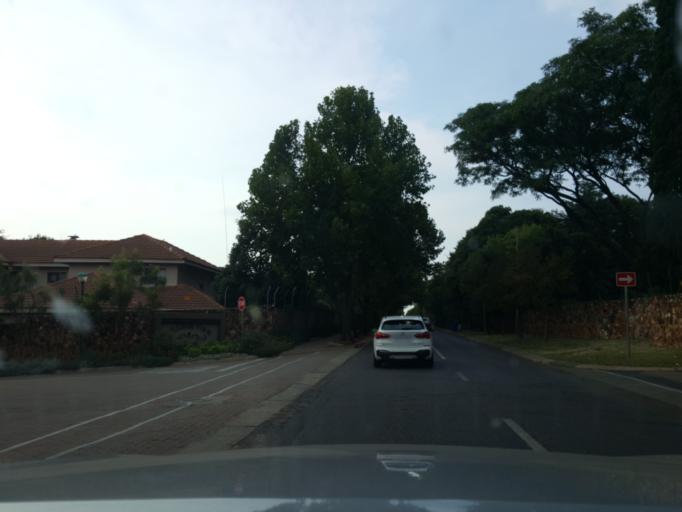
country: ZA
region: Gauteng
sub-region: City of Tshwane Metropolitan Municipality
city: Centurion
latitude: -25.8702
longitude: 28.2126
